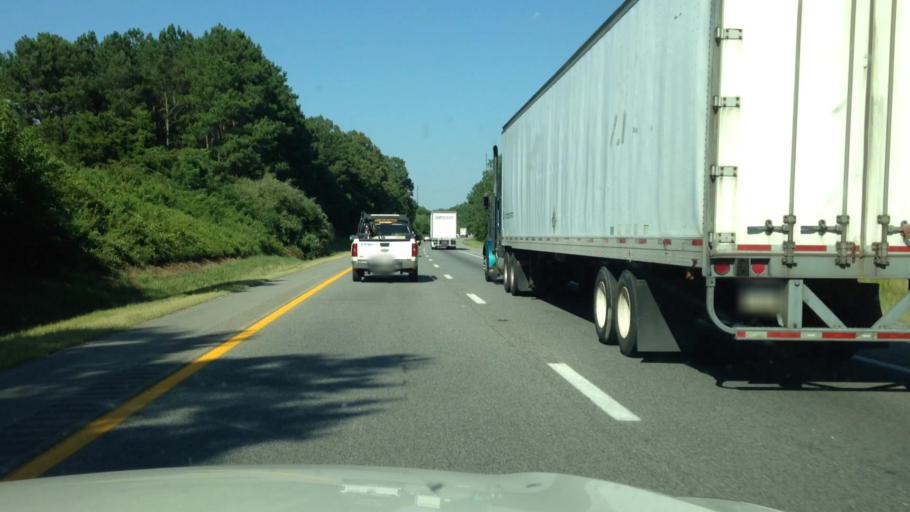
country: US
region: Virginia
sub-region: City of Emporia
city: Emporia
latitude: 36.7622
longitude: -77.4936
